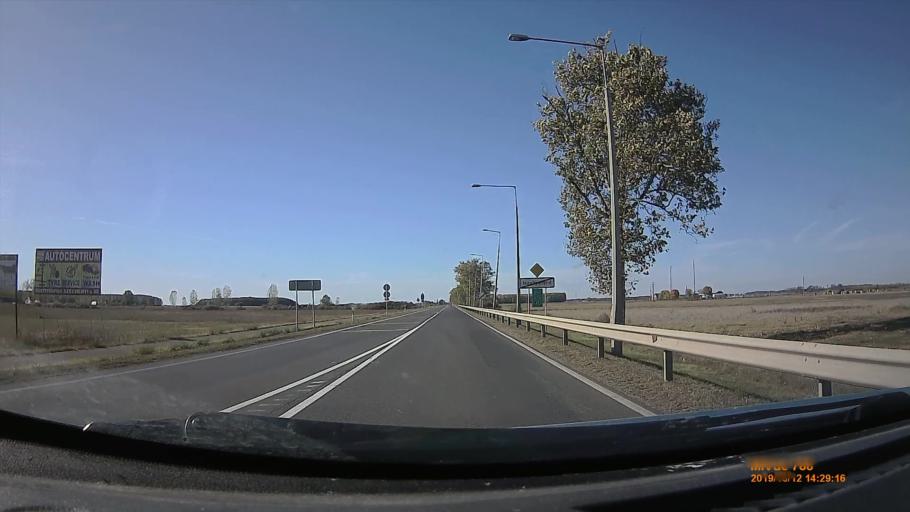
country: HU
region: Hajdu-Bihar
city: Berettyoujfalu
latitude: 47.1694
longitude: 21.6154
